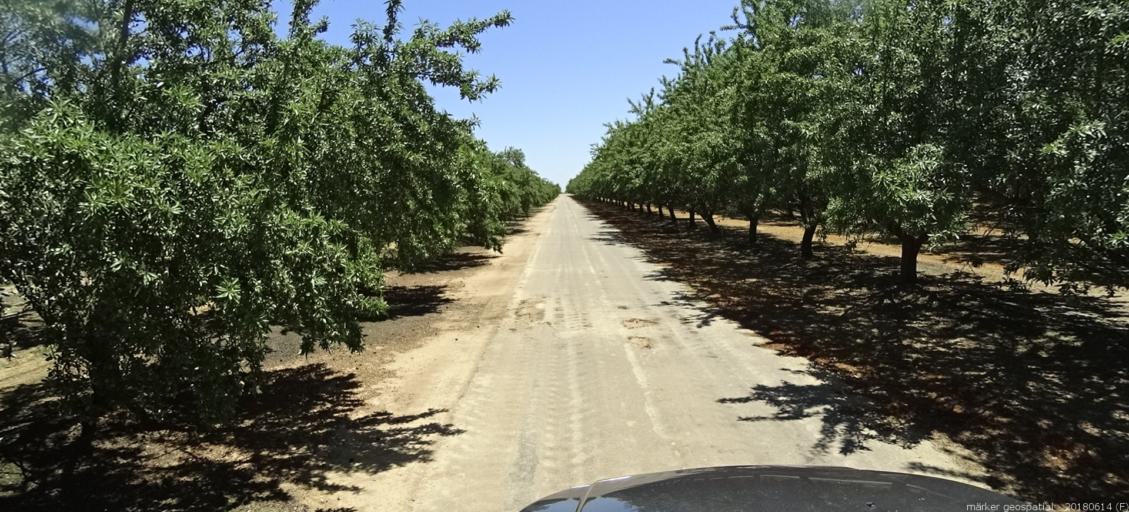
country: US
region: California
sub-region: Madera County
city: Fairmead
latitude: 37.0474
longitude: -120.1874
